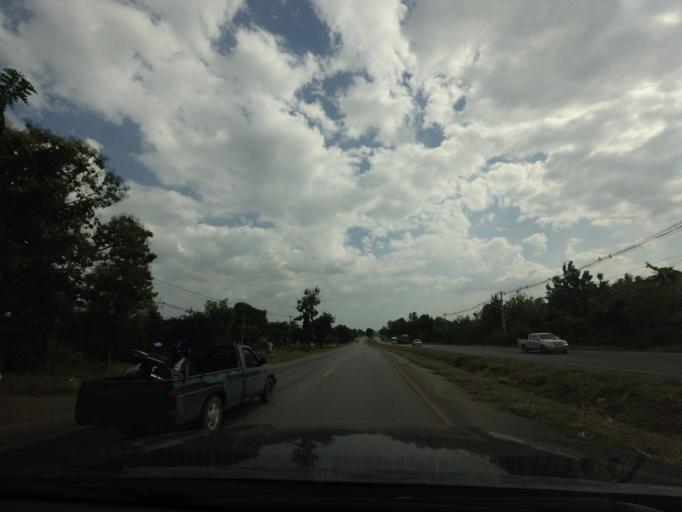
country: TH
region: Lop Buri
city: Chai Badan
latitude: 15.2408
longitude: 101.1262
